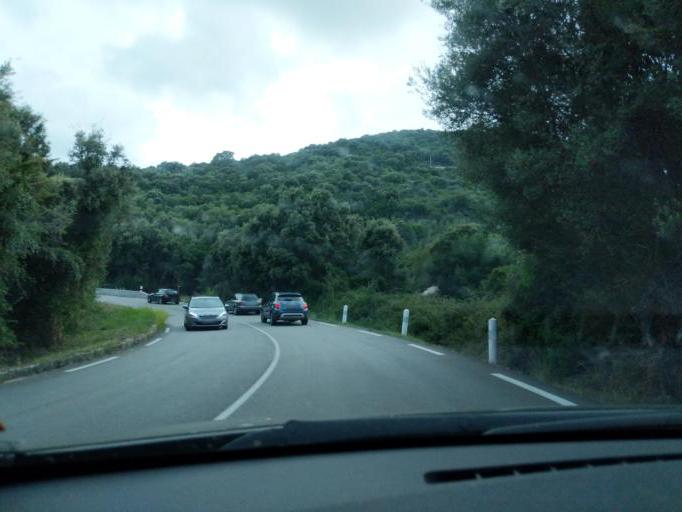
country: FR
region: Corsica
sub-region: Departement de la Corse-du-Sud
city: Sartene
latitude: 41.5802
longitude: 8.9478
